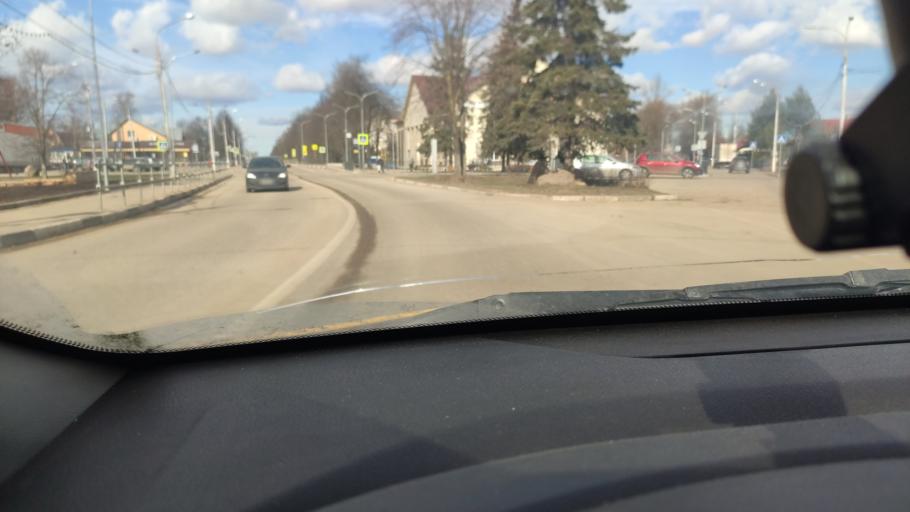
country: RU
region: Moskovskaya
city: Ruza
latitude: 55.7037
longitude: 36.1902
